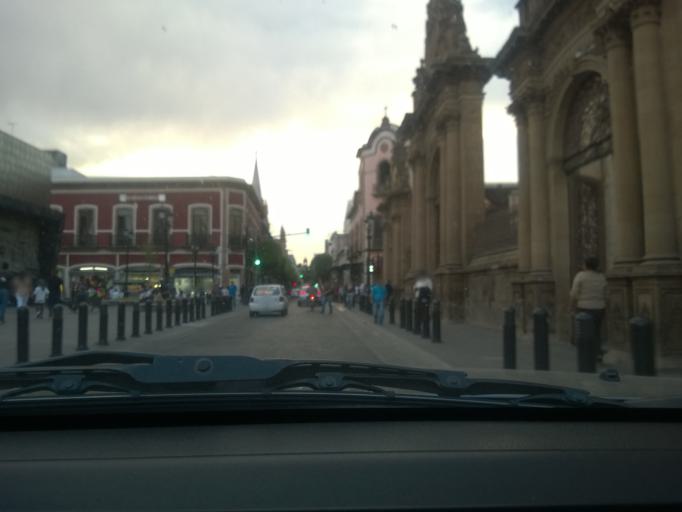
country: MX
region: Guanajuato
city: Leon
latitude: 21.1238
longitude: -101.6819
